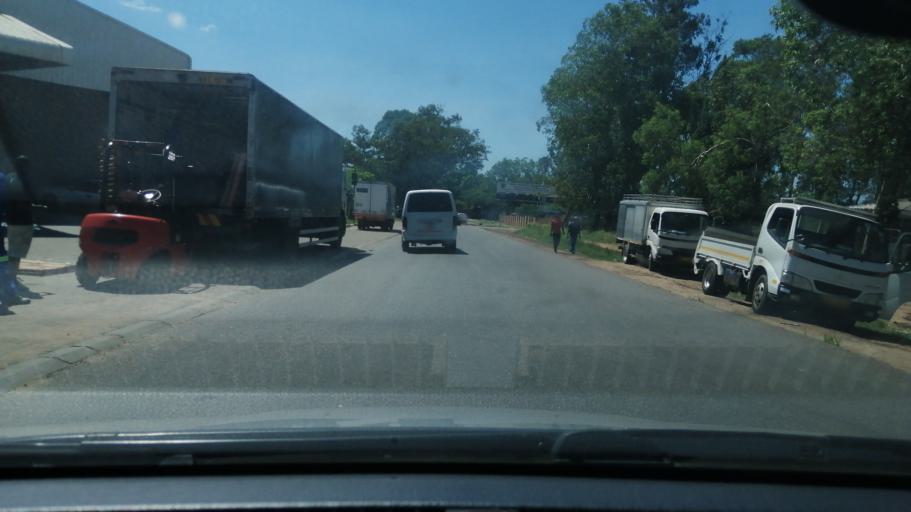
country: ZW
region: Harare
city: Epworth
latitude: -17.8401
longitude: 31.1199
